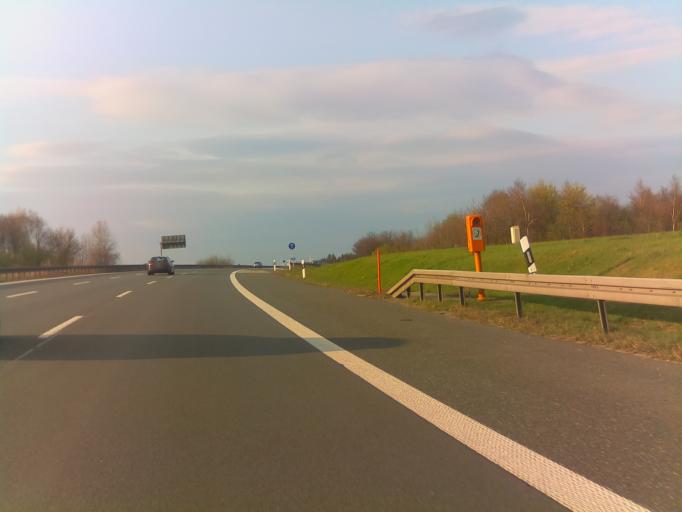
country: DE
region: Bavaria
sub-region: Upper Franconia
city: Munchberg
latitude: 50.1678
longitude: 11.7457
